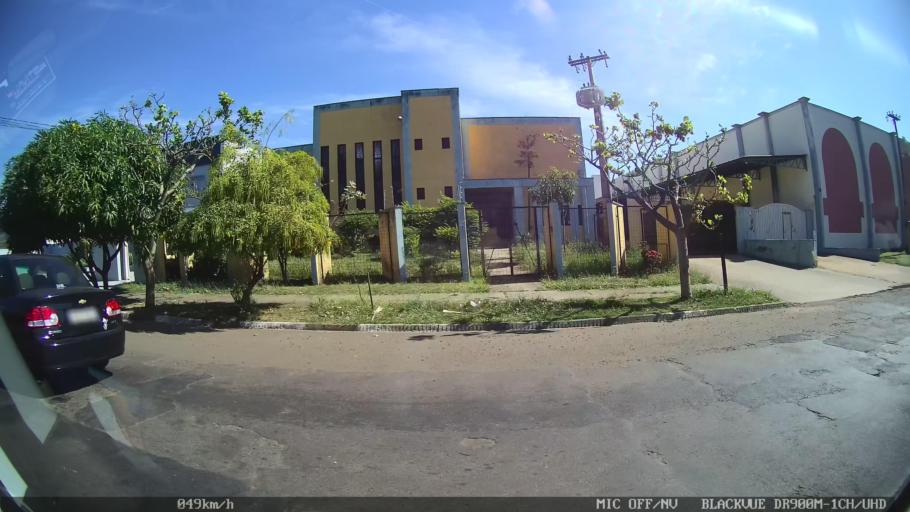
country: BR
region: Sao Paulo
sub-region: Franca
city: Franca
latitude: -20.5495
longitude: -47.4371
